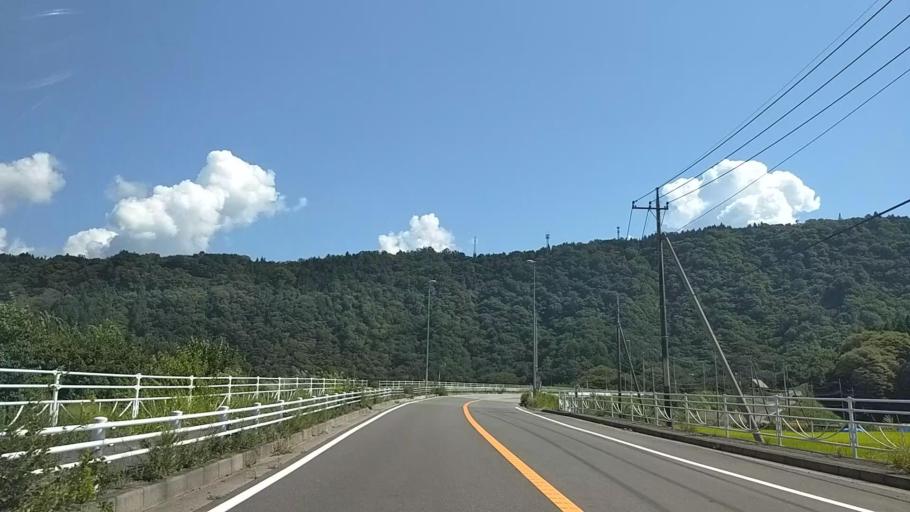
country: JP
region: Yamanashi
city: Ryuo
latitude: 35.5137
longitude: 138.4561
